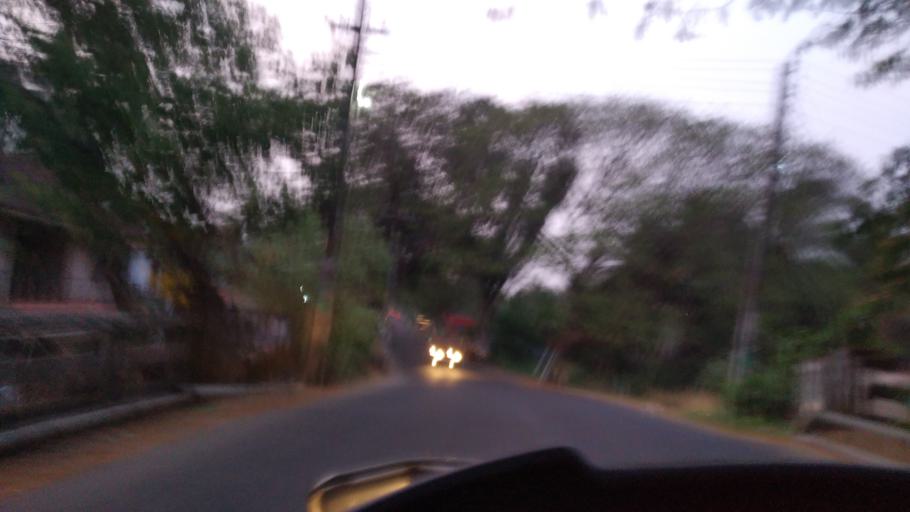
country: IN
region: Kerala
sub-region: Kottayam
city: Kottayam
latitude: 9.6152
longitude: 76.4328
